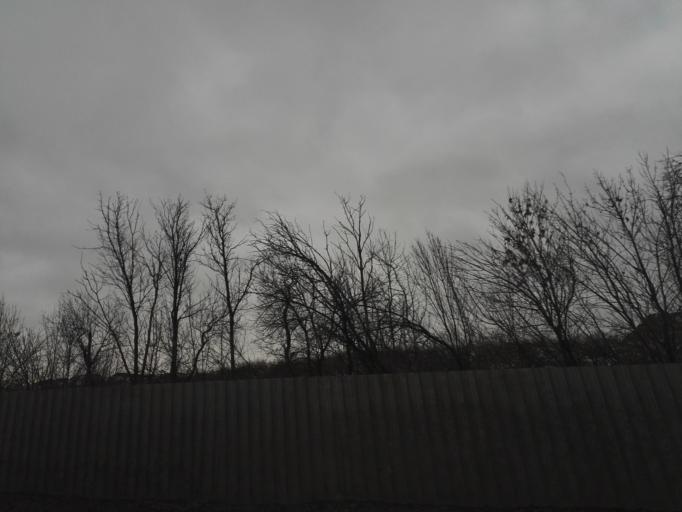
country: RU
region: Tula
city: Tula
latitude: 54.1431
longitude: 37.6574
